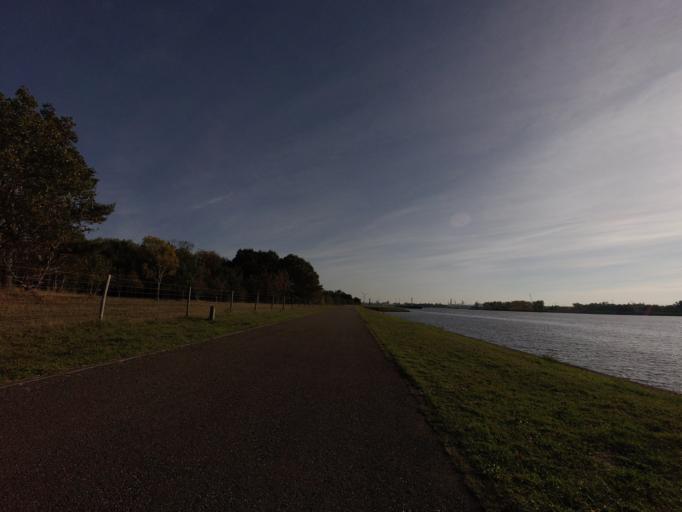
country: BE
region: Flanders
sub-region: Provincie Antwerpen
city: Stabroek
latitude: 51.3365
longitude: 4.3049
